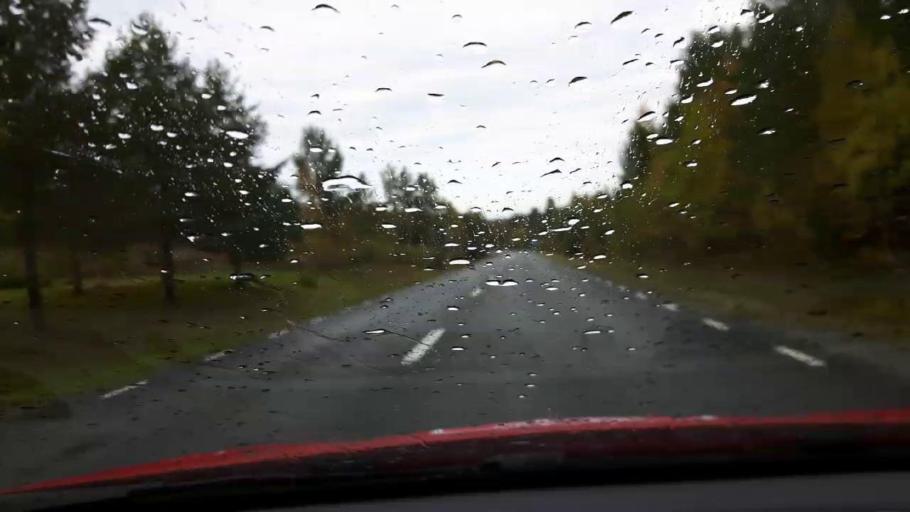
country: SE
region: Jaemtland
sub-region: Krokoms Kommun
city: Krokom
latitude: 63.1204
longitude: 14.2937
